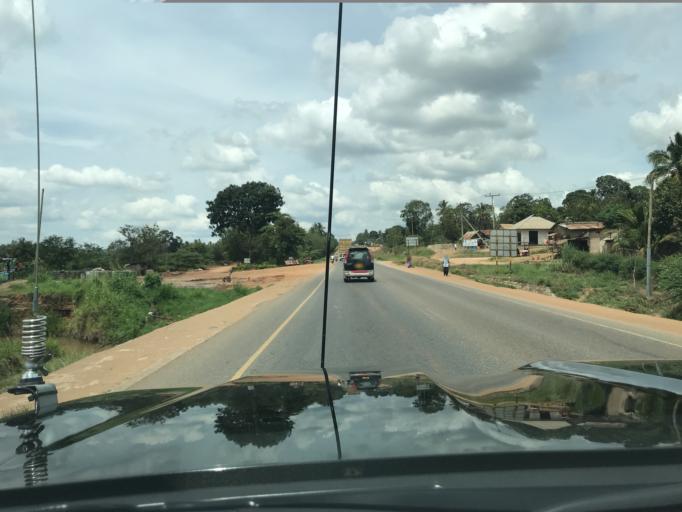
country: TZ
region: Pwani
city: Kibaha
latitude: -6.7629
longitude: 38.9484
